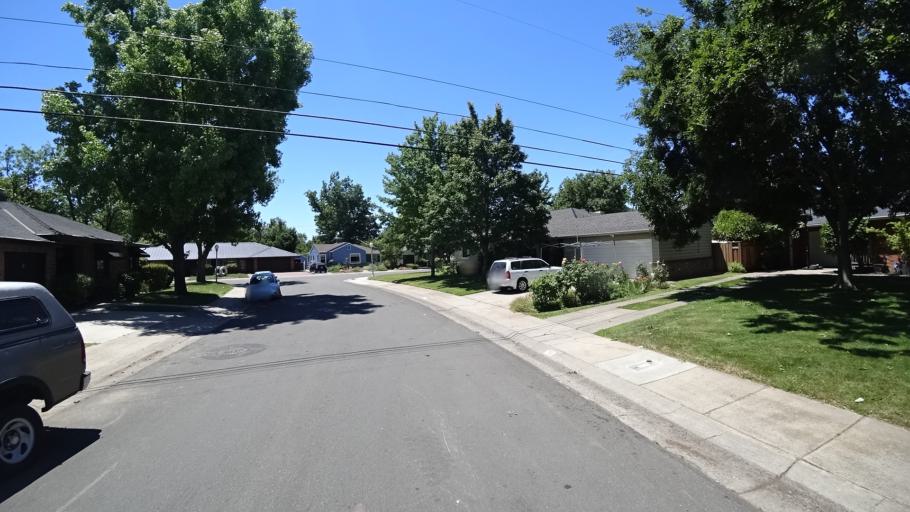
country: US
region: California
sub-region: Sacramento County
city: Sacramento
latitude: 38.5792
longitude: -121.4453
